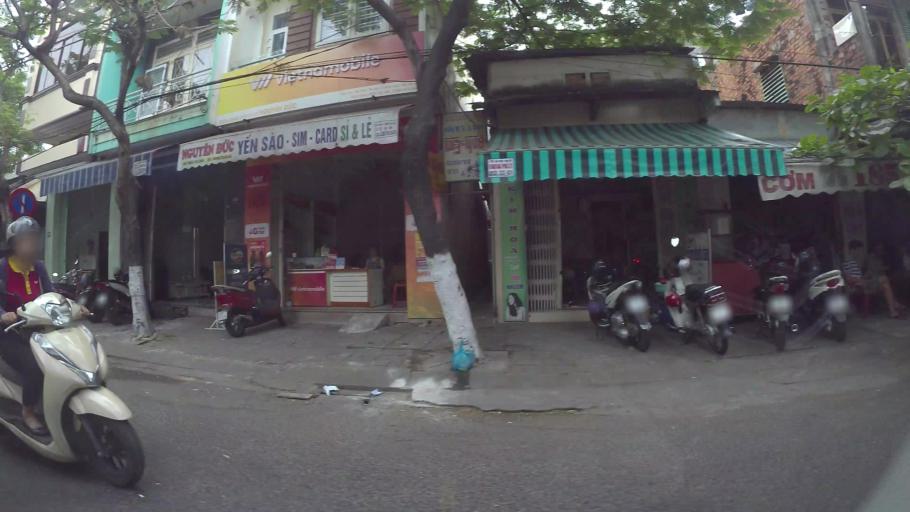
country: VN
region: Da Nang
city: Thanh Khe
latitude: 16.0685
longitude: 108.1960
